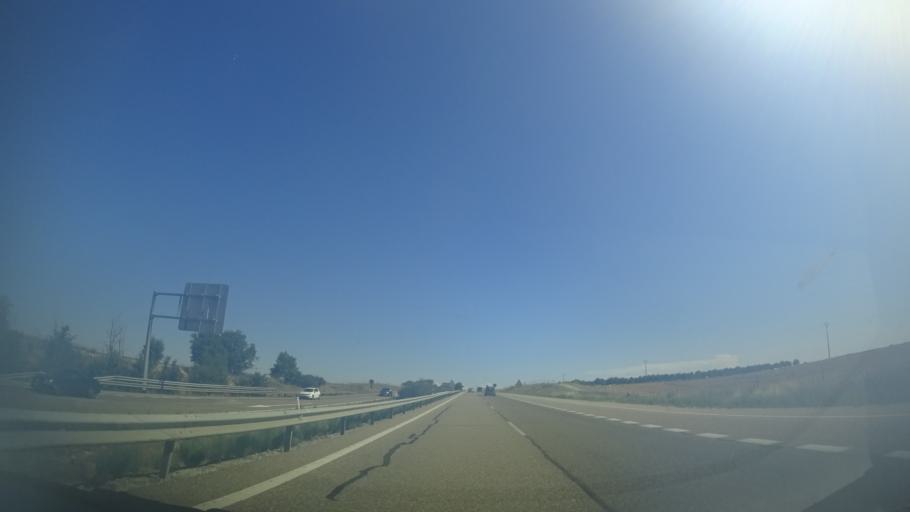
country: ES
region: Castille and Leon
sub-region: Provincia de Valladolid
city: Uruena
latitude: 41.6762
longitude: -5.2049
